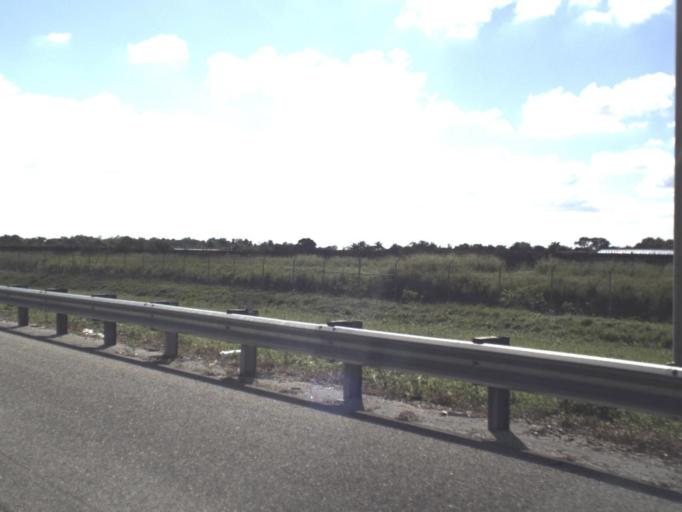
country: US
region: Florida
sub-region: Palm Beach County
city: Villages of Oriole
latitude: 26.4717
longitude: -80.1746
